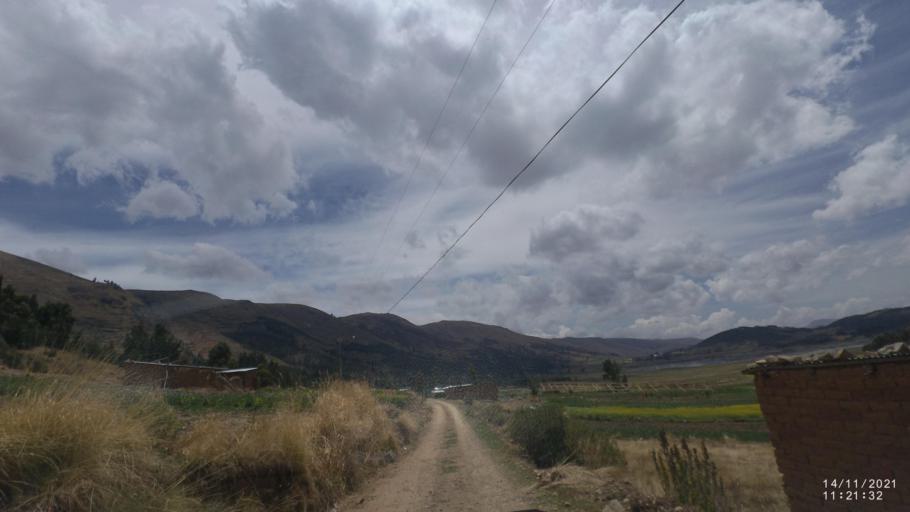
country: BO
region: Cochabamba
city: Cochabamba
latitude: -17.3364
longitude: -66.0358
